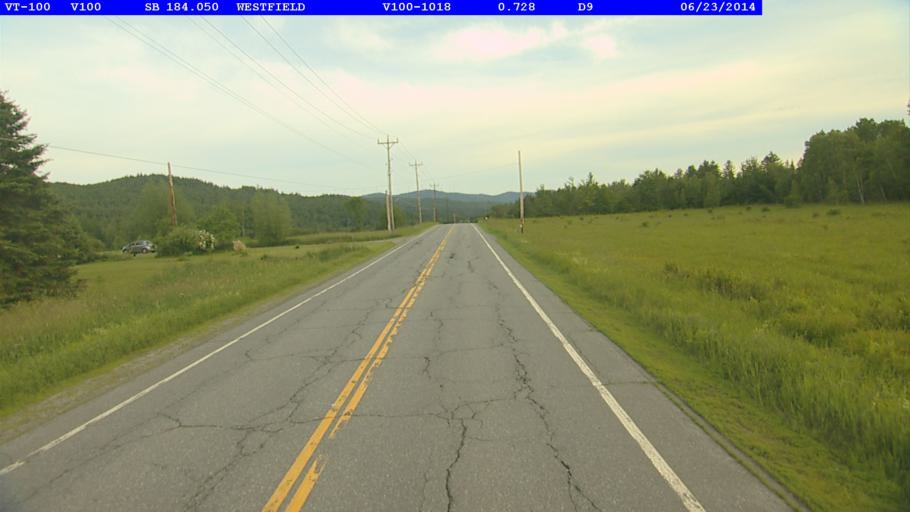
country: US
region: Vermont
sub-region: Orleans County
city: Newport
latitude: 44.8456
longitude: -72.4340
